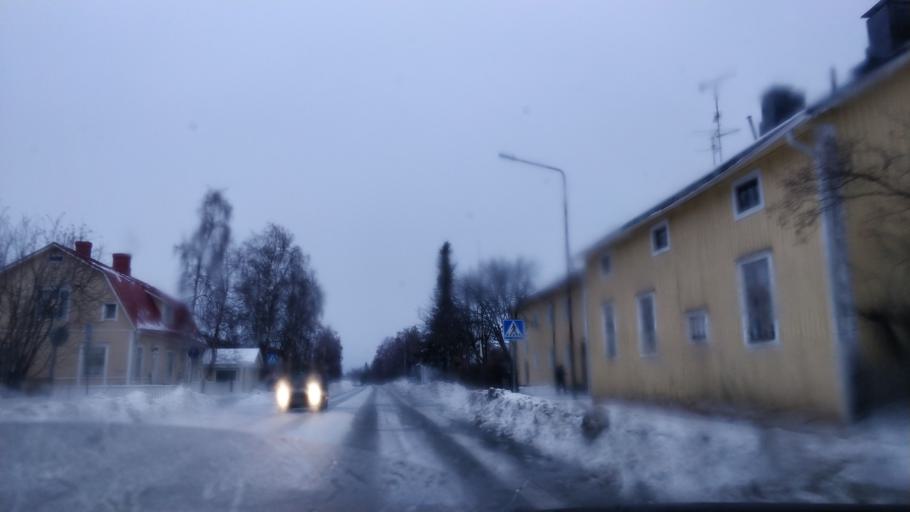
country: FI
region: Lapland
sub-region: Kemi-Tornio
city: Kemi
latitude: 65.7403
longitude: 24.5606
